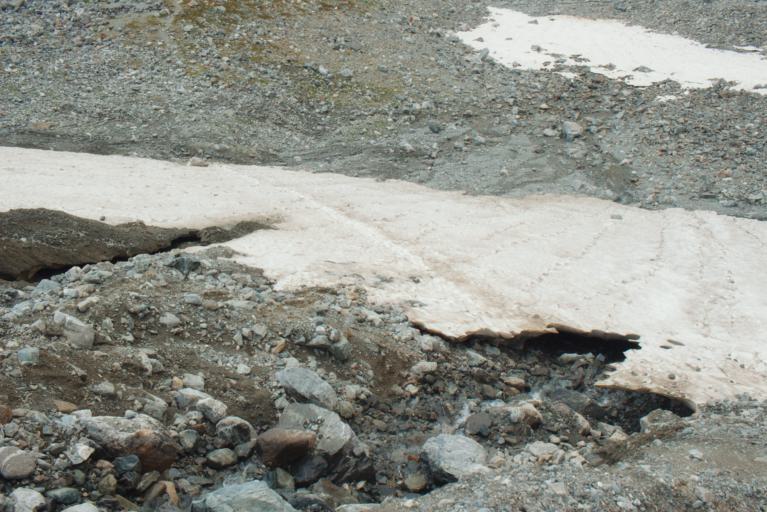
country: RU
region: Karachayevo-Cherkesiya
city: Nizhniy Arkhyz
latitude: 43.4299
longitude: 41.2566
